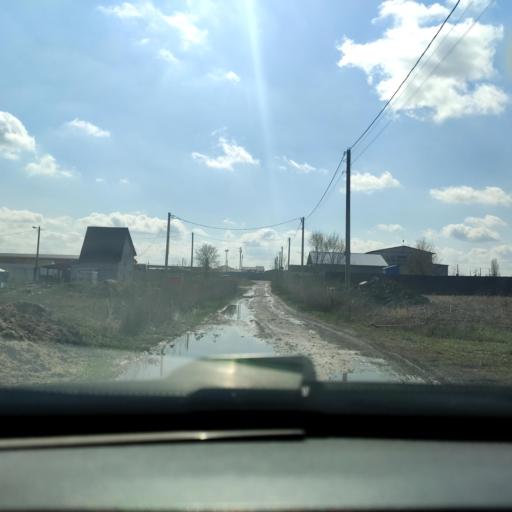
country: RU
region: Voronezj
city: Somovo
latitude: 51.6706
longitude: 39.3339
